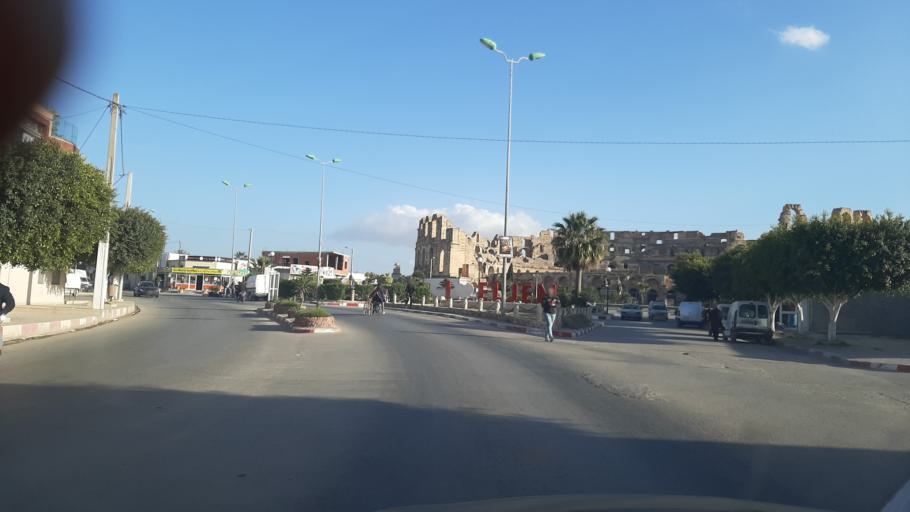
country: TN
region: Al Mahdiyah
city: El Jem
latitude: 35.2983
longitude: 10.7057
